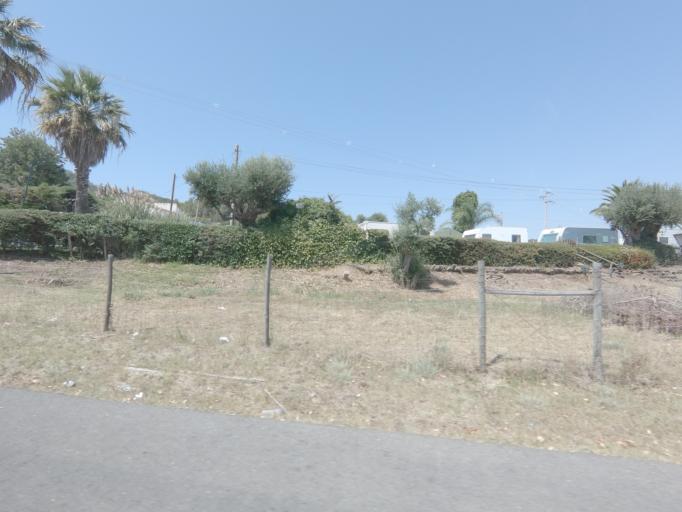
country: PT
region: Setubal
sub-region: Setubal
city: Setubal
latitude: 38.5320
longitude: -8.9150
